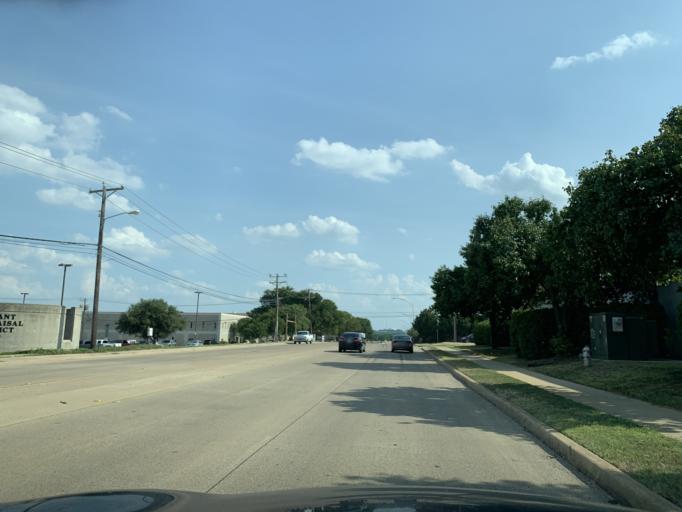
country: US
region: Texas
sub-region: Tarrant County
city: Richland Hills
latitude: 32.7957
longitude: -97.2213
